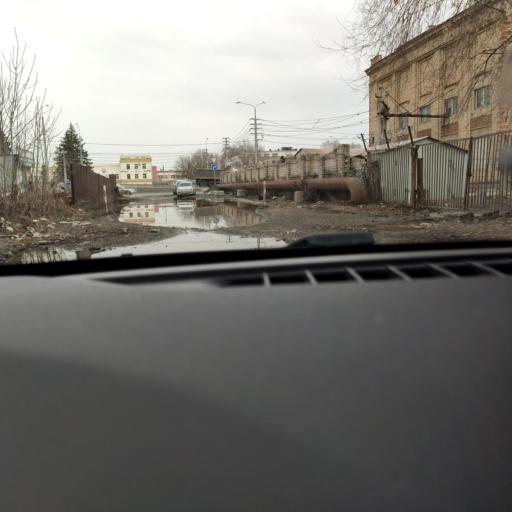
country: RU
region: Samara
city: Smyshlyayevka
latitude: 53.2070
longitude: 50.2736
